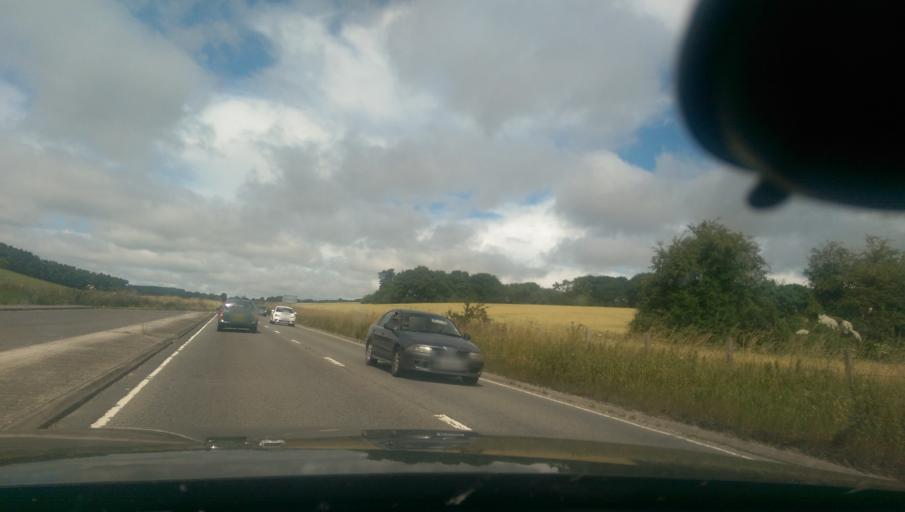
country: GB
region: England
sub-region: Wiltshire
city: Chicklade
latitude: 51.1091
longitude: -2.1025
